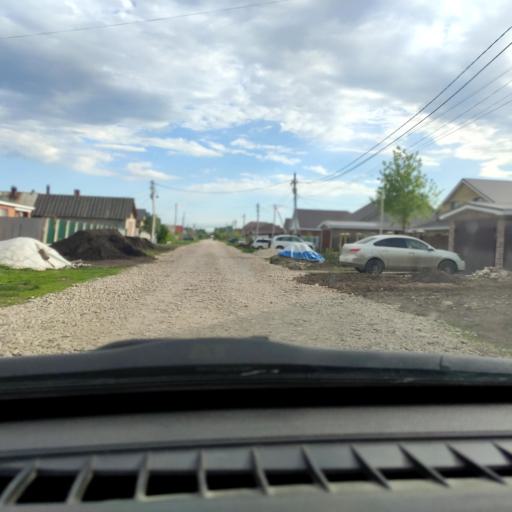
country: RU
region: Samara
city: Tol'yatti
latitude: 53.5652
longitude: 49.4074
